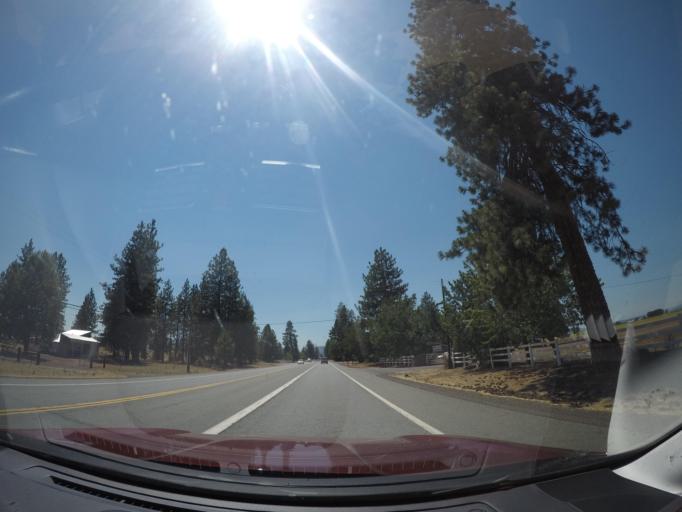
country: US
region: California
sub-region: Shasta County
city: Burney
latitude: 41.0595
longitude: -121.3742
